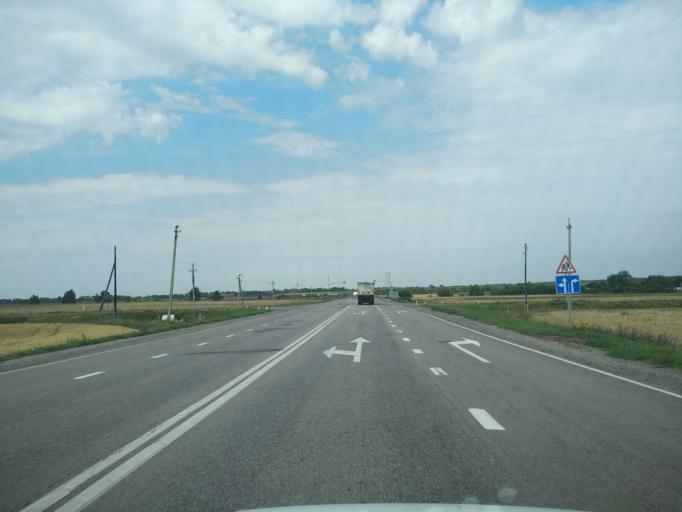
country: RU
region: Voronezj
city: Verkhnyaya Khava
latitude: 51.6781
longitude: 39.8776
